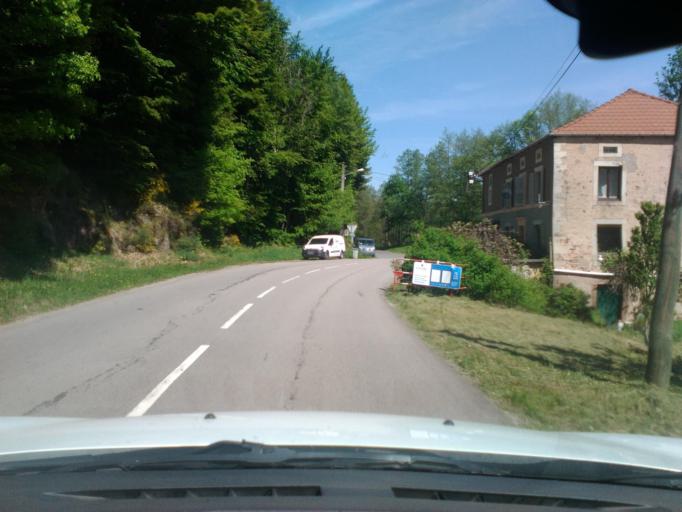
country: FR
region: Lorraine
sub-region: Departement des Vosges
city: Bruyeres
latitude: 48.2460
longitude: 6.7292
